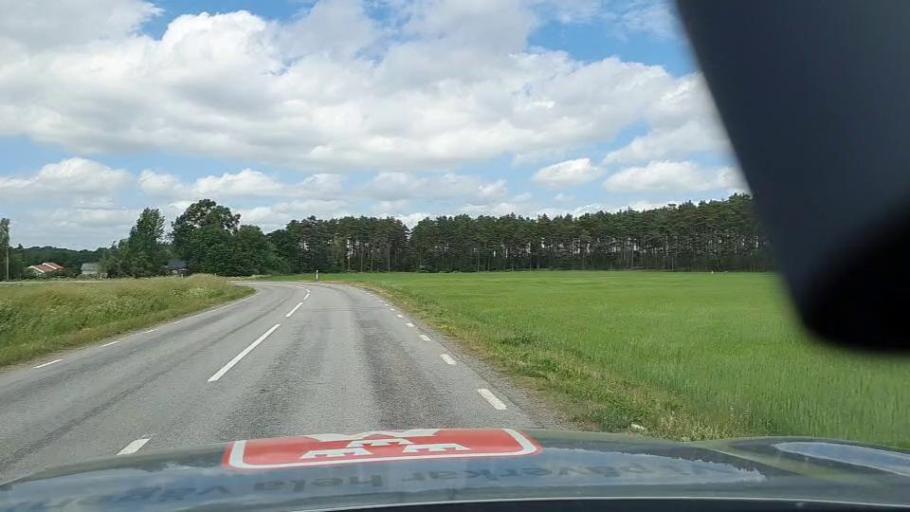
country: SE
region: Blekinge
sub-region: Karlshamns Kommun
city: Morrum
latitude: 56.0887
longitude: 14.7058
